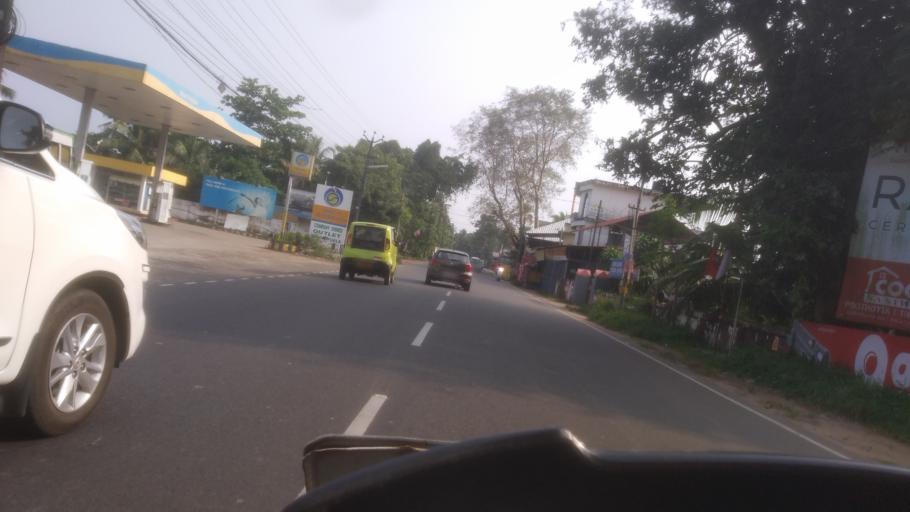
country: IN
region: Kerala
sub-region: Alappuzha
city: Arukutti
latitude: 9.8867
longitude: 76.3741
